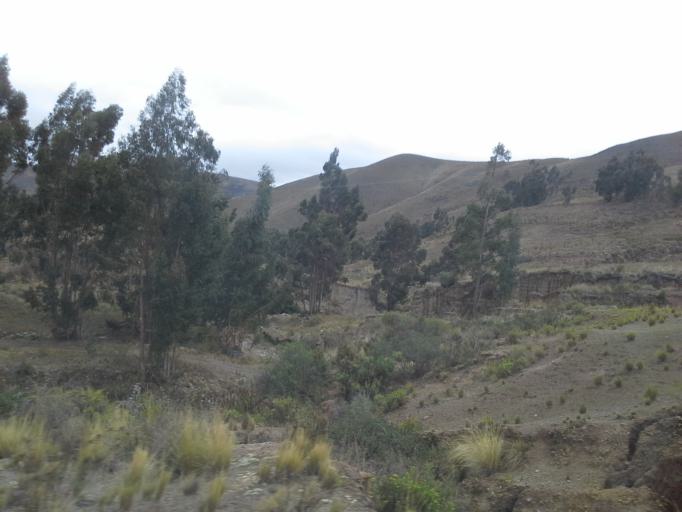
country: BO
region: Cochabamba
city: Colomi
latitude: -17.4169
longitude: -65.8029
